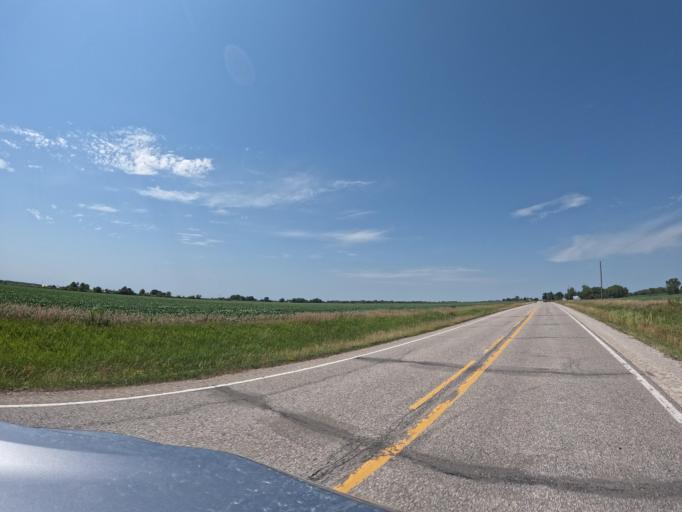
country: US
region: Iowa
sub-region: Henry County
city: Mount Pleasant
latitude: 40.8991
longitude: -91.6221
